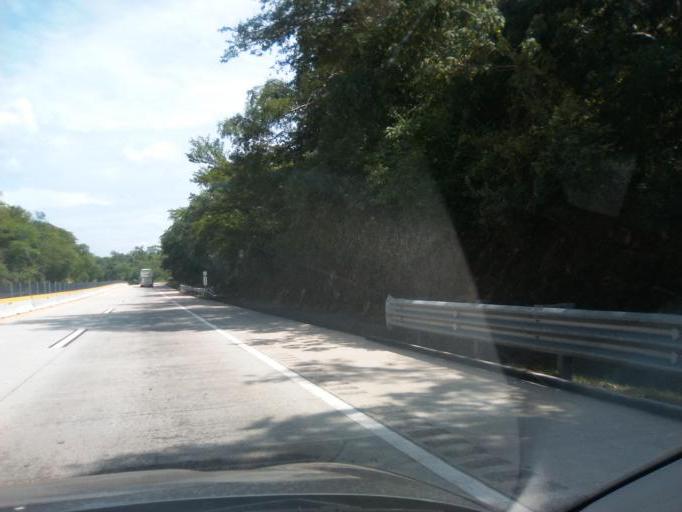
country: MX
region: Guerrero
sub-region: Acapulco de Juarez
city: Colonia Nueva Revolucion
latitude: 16.9293
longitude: -99.7949
